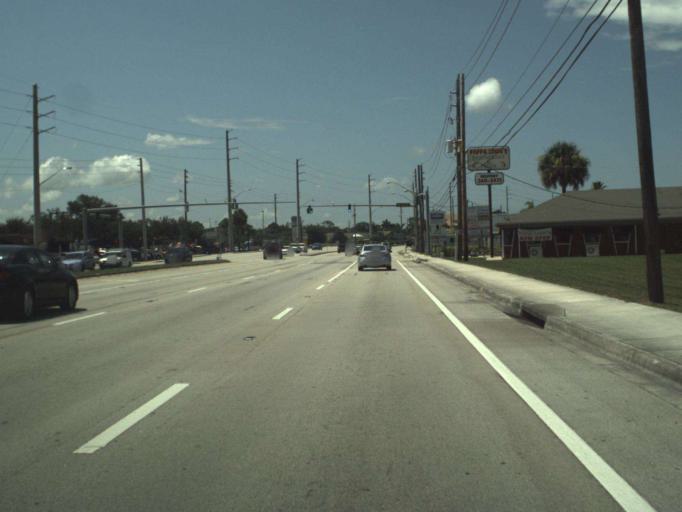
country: US
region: Florida
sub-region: Saint Lucie County
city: River Park
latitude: 27.3329
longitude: -80.3243
